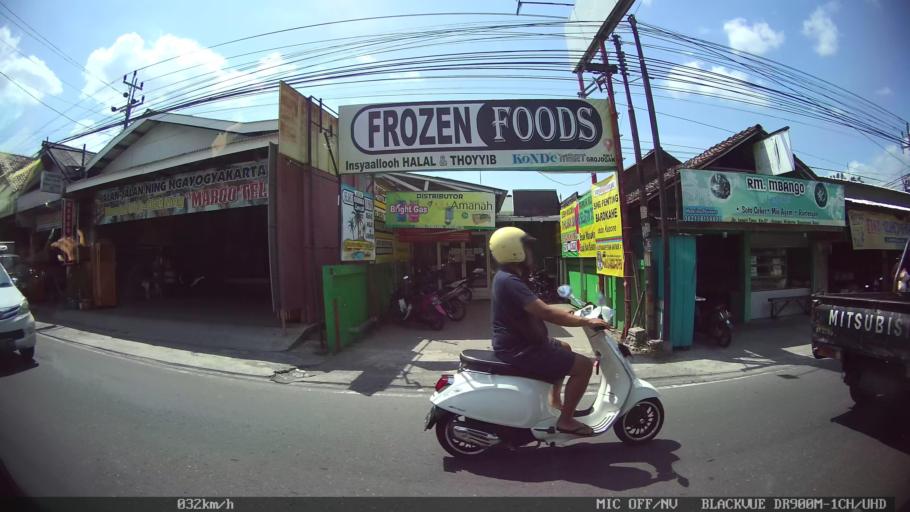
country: ID
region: Daerah Istimewa Yogyakarta
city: Sewon
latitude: -7.8446
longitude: 110.3911
